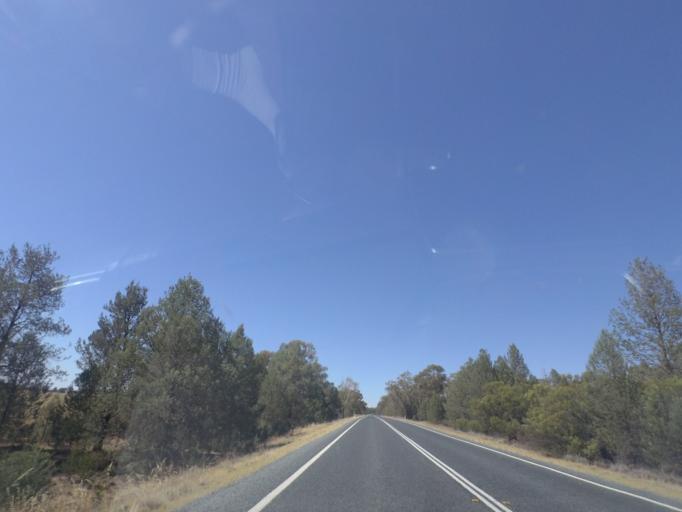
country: AU
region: New South Wales
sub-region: Narrandera
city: Narrandera
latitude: -34.4335
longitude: 146.8427
